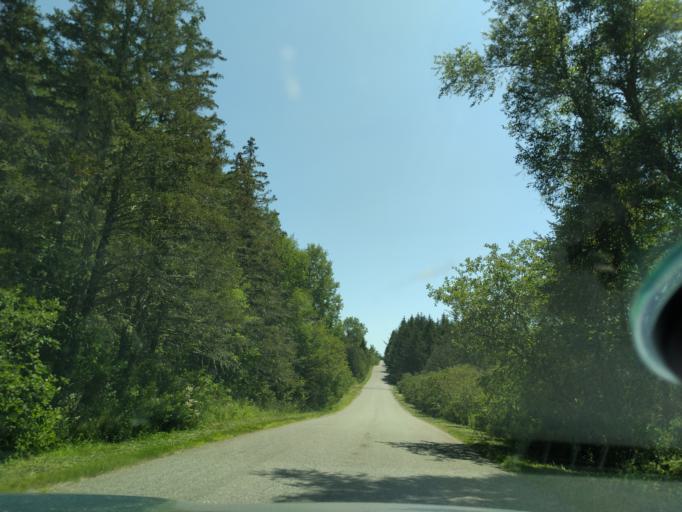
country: US
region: Maine
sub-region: Washington County
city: Eastport
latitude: 44.8357
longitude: -67.0104
